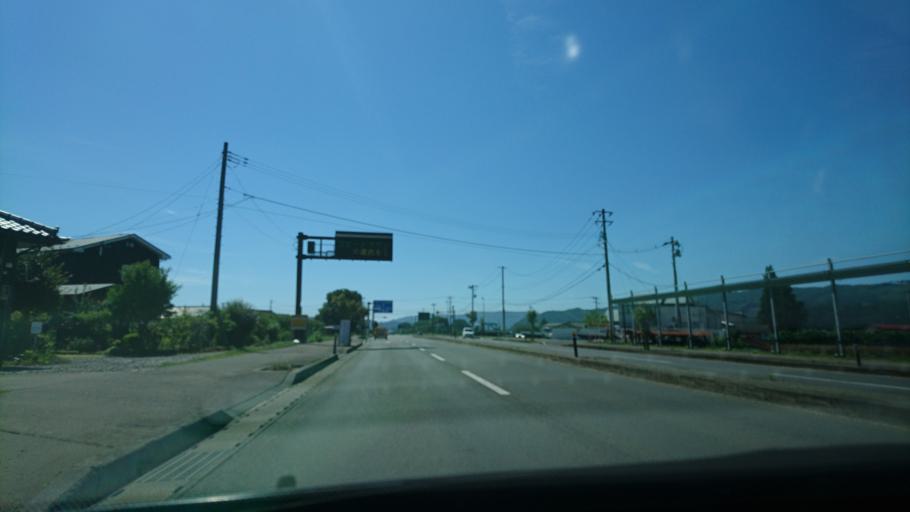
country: JP
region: Iwate
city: Tono
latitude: 39.3267
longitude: 141.5639
